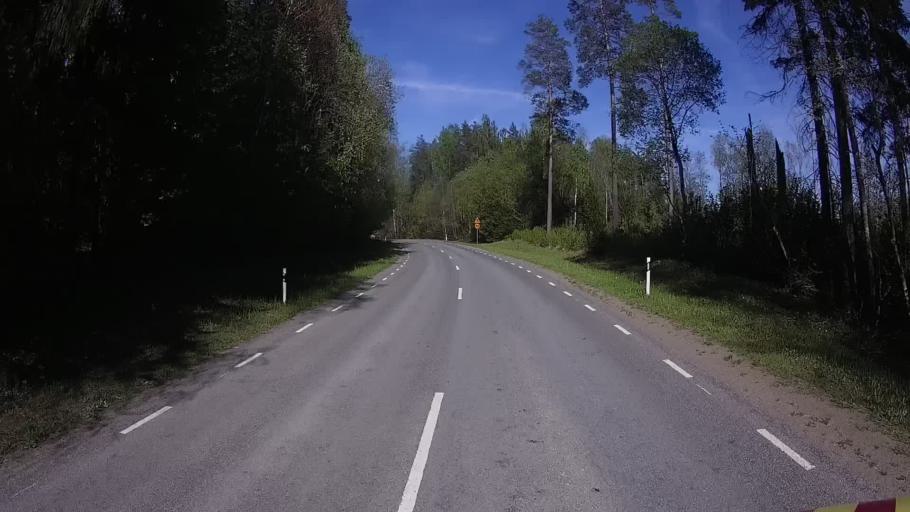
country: EE
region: Vorumaa
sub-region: Antsla vald
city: Vana-Antsla
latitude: 57.9464
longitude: 26.3954
